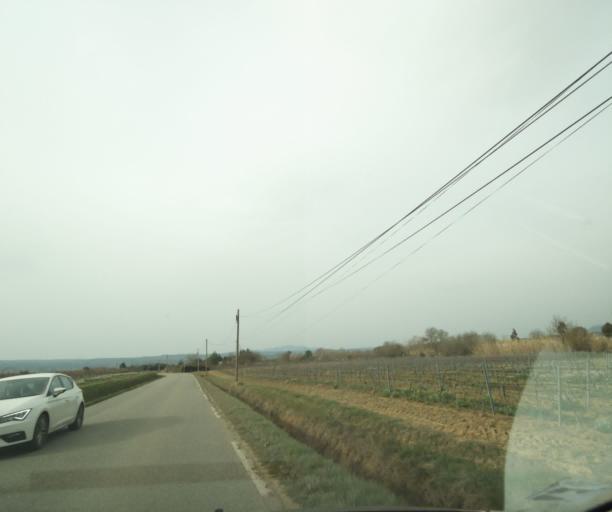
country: FR
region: Provence-Alpes-Cote d'Azur
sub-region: Departement des Bouches-du-Rhone
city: Trets
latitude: 43.4718
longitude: 5.7119
